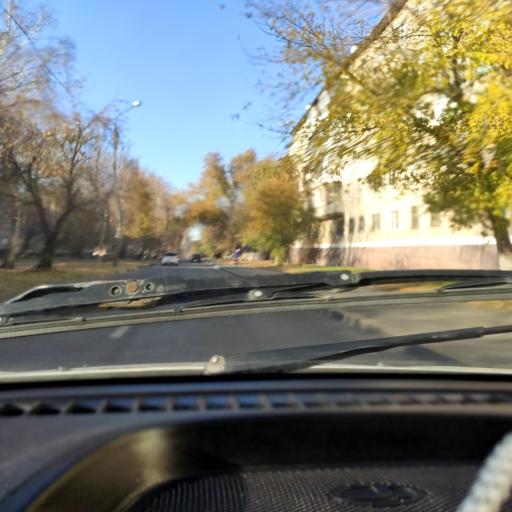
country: RU
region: Samara
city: Tol'yatti
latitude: 53.5198
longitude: 49.4028
